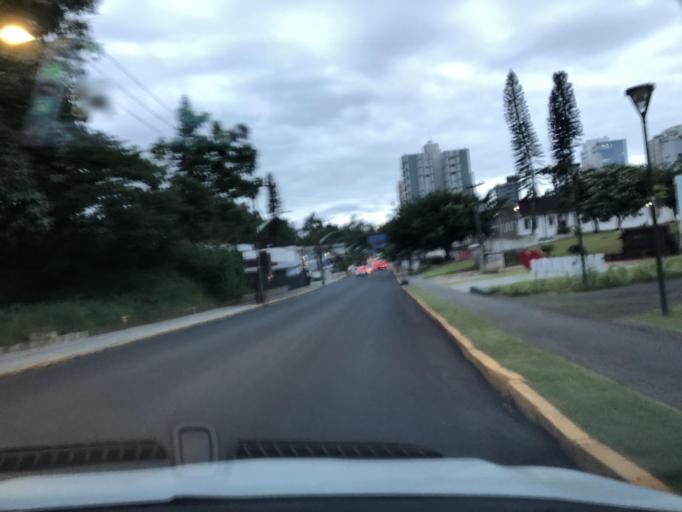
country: BR
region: Santa Catarina
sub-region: Joinville
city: Joinville
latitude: -26.2985
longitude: -48.8569
